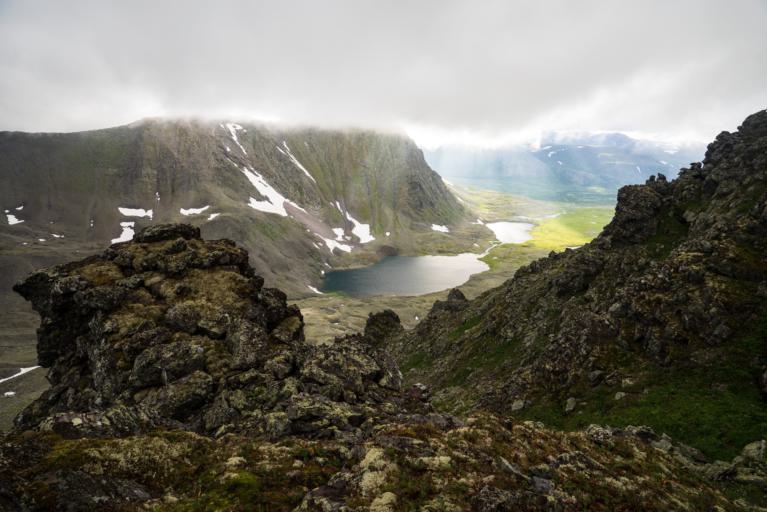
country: RU
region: Komi Republic
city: Synya
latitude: 64.8132
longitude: 59.2221
